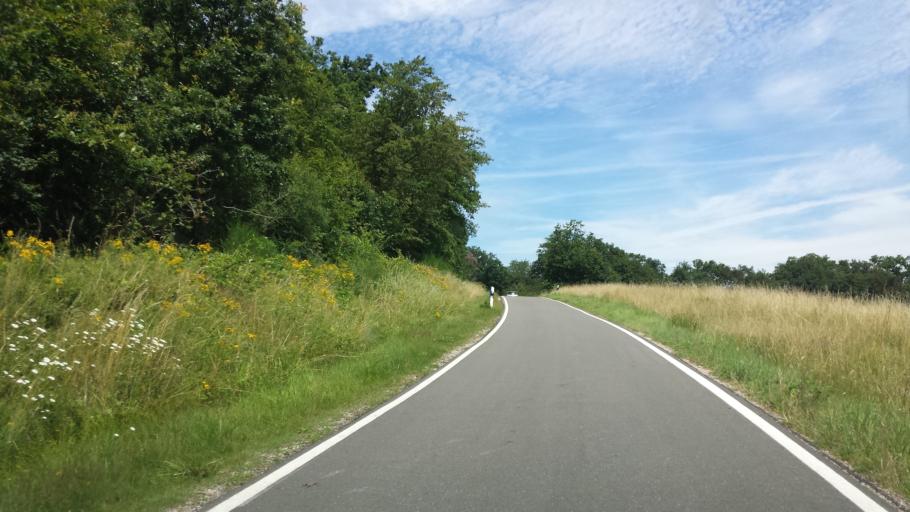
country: DE
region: Rheinland-Pfalz
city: Dreisen
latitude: 49.5719
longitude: 8.0202
